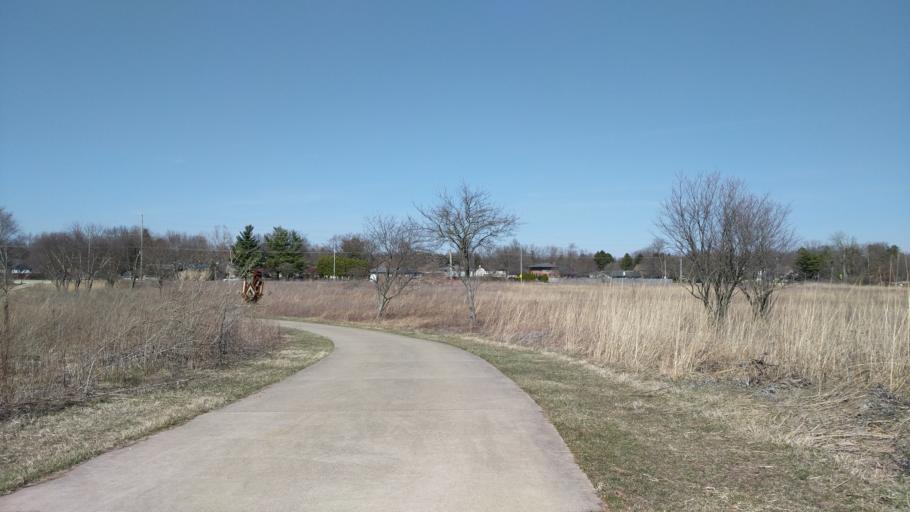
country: US
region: Illinois
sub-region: Champaign County
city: Urbana
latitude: 40.0820
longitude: -88.2047
